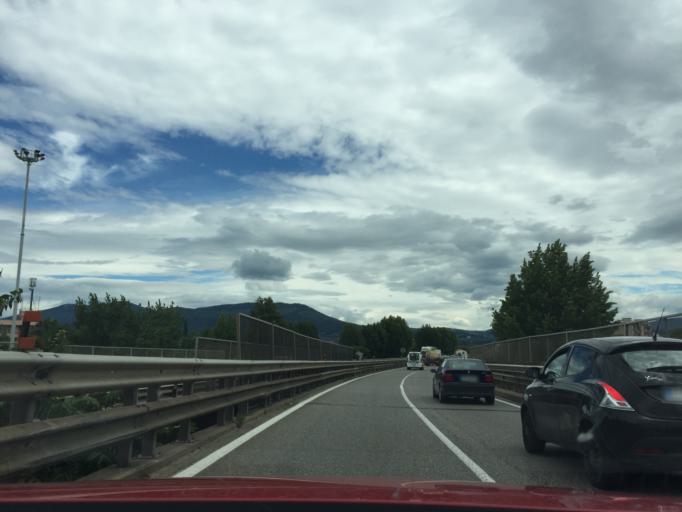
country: IT
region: Tuscany
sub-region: Province of Florence
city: Mantignano-Ugnano
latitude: 43.7936
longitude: 11.1990
